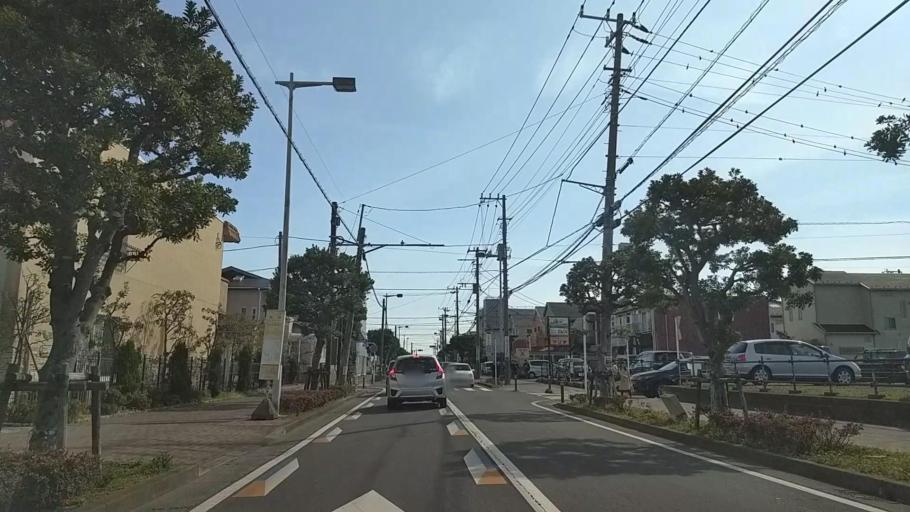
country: JP
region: Kanagawa
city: Fujisawa
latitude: 35.3278
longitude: 139.4476
